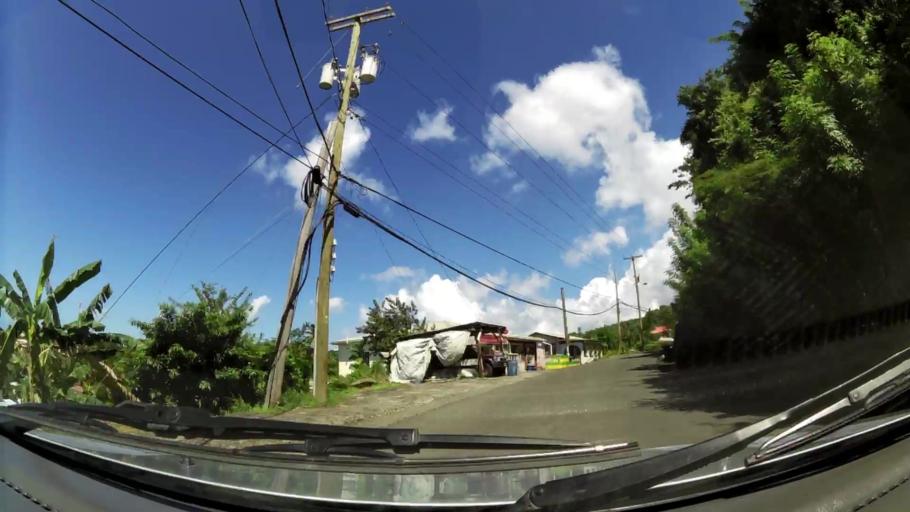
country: GD
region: Saint John
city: Gouyave
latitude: 12.1215
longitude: -61.7448
